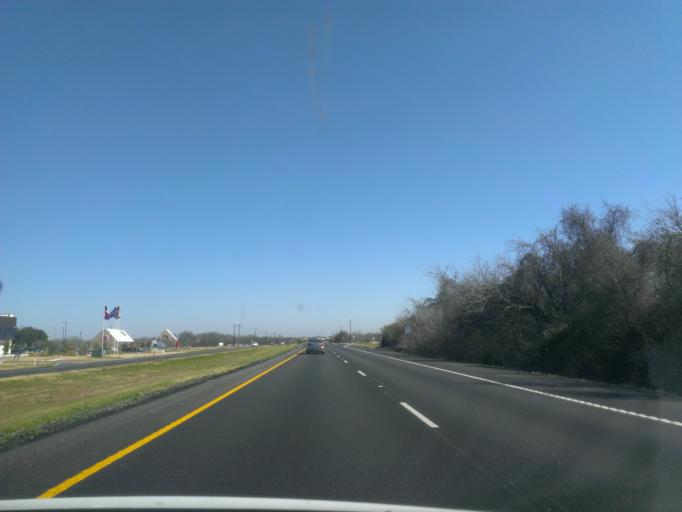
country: US
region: Texas
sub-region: Williamson County
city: Round Rock
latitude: 30.5269
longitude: -97.6272
